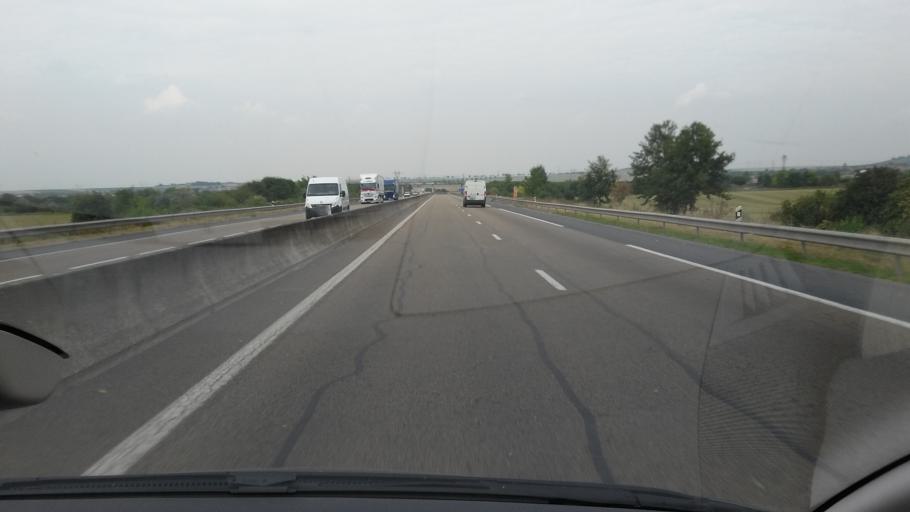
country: FR
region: Champagne-Ardenne
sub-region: Departement de la Marne
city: Cernay-les-Reims
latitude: 49.2471
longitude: 4.0820
